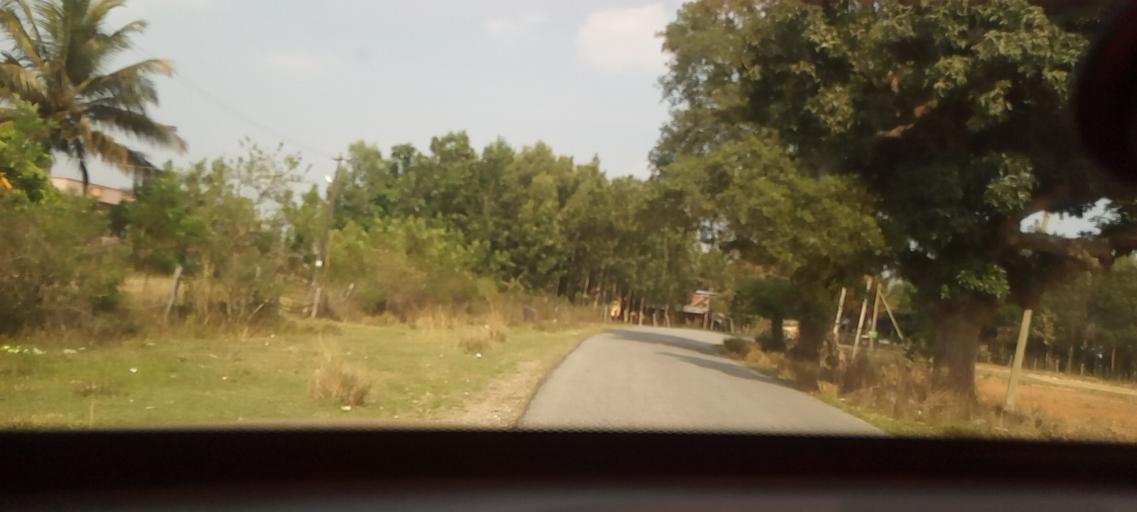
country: IN
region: Karnataka
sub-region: Hassan
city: Belur
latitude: 13.1834
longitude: 75.8355
